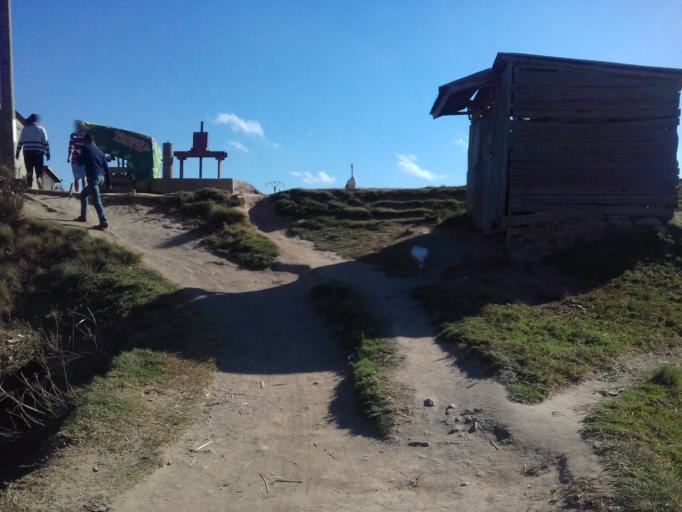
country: MG
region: Analamanga
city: Antananarivo
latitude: -18.8886
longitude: 47.4862
